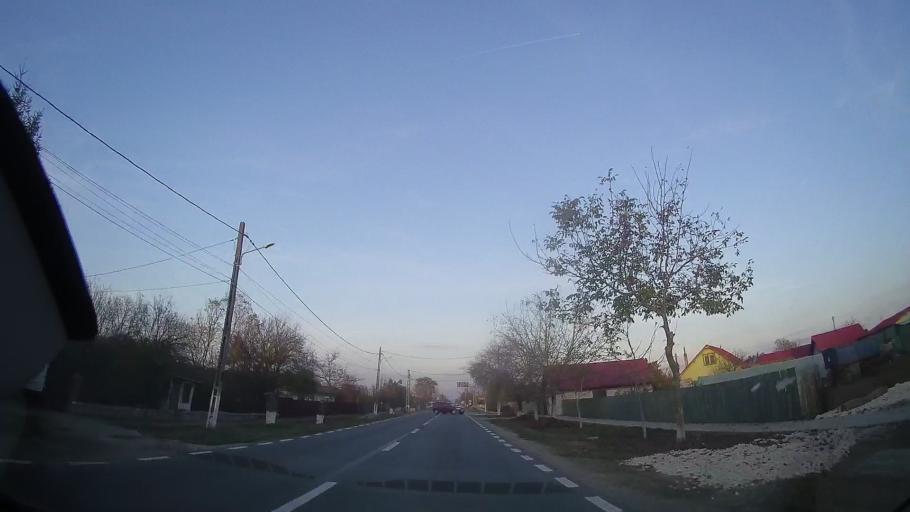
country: RO
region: Constanta
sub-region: Comuna Topraisar
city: Topraisar
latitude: 44.0091
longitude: 28.4458
